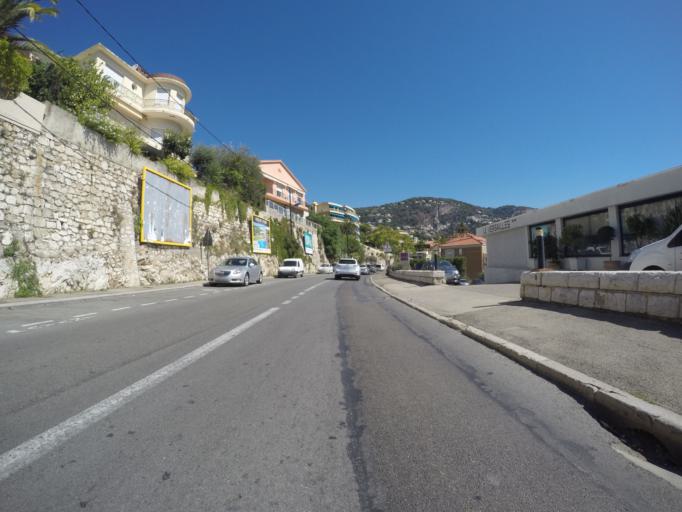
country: FR
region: Provence-Alpes-Cote d'Azur
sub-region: Departement des Alpes-Maritimes
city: Villefranche-sur-Mer
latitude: 43.7003
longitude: 7.3056
